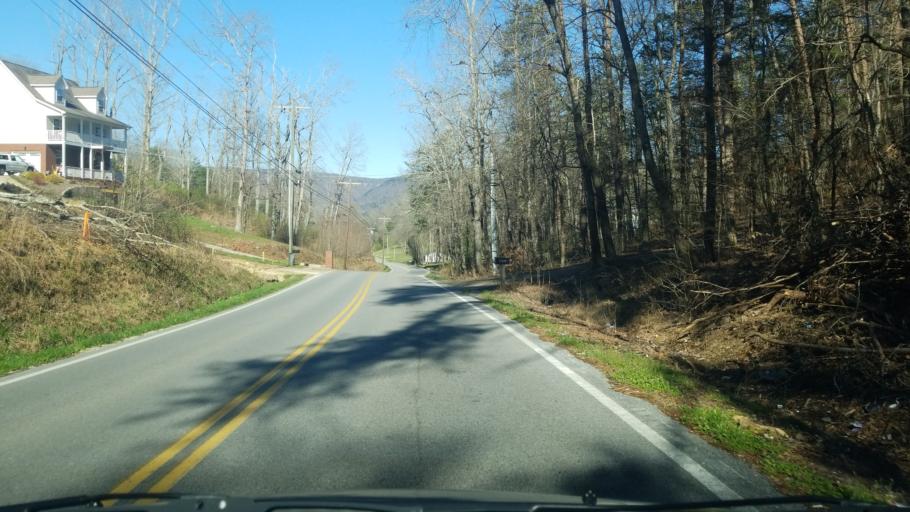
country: US
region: Tennessee
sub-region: Hamilton County
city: Soddy-Daisy
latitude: 35.2192
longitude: -85.1888
